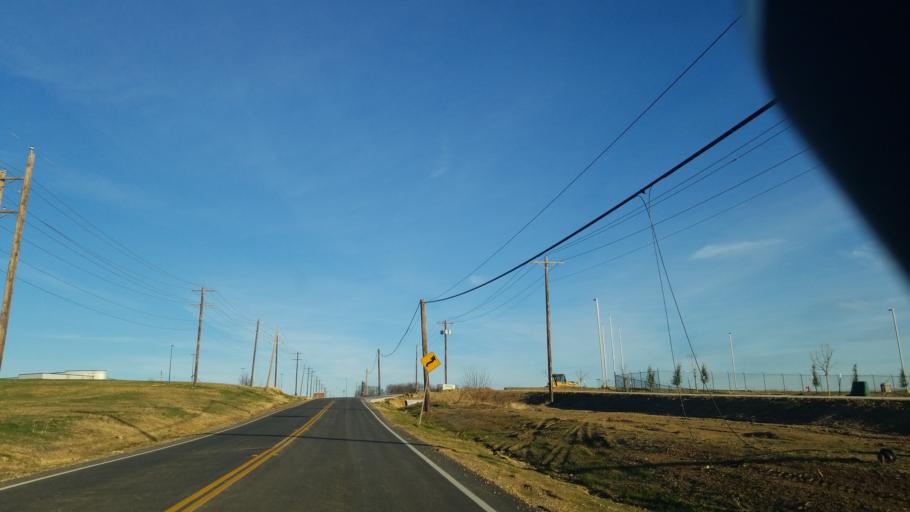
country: US
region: Texas
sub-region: Denton County
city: Denton
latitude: 33.2193
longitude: -97.1802
